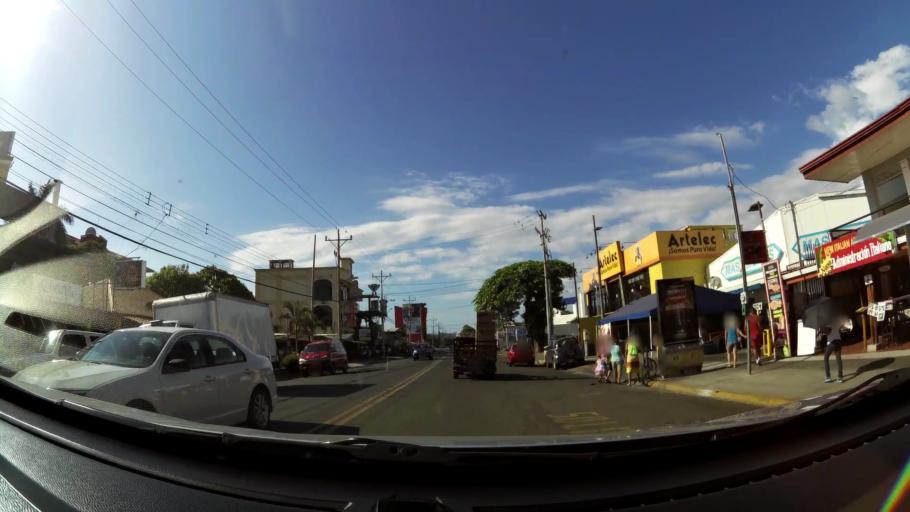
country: CR
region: Puntarenas
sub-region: Canton de Garabito
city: Jaco
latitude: 9.6129
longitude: -84.6267
